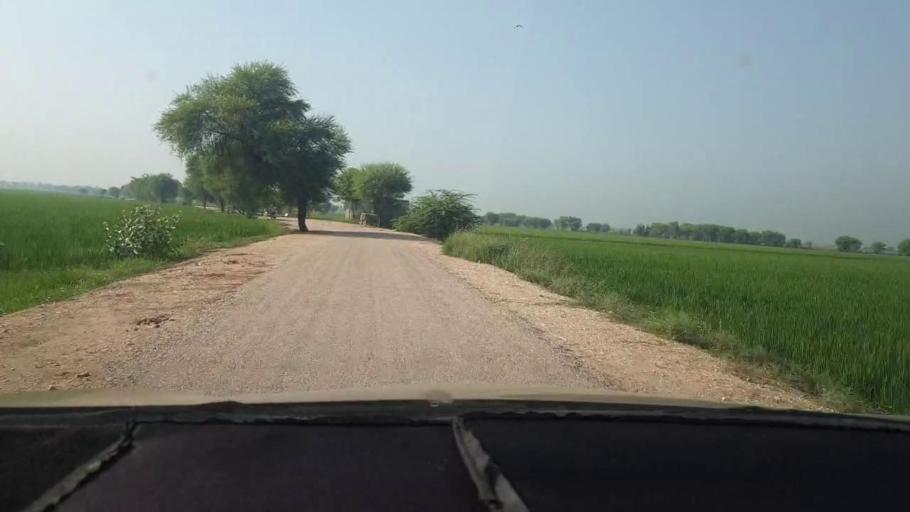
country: PK
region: Sindh
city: Kambar
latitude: 27.6262
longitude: 68.0893
